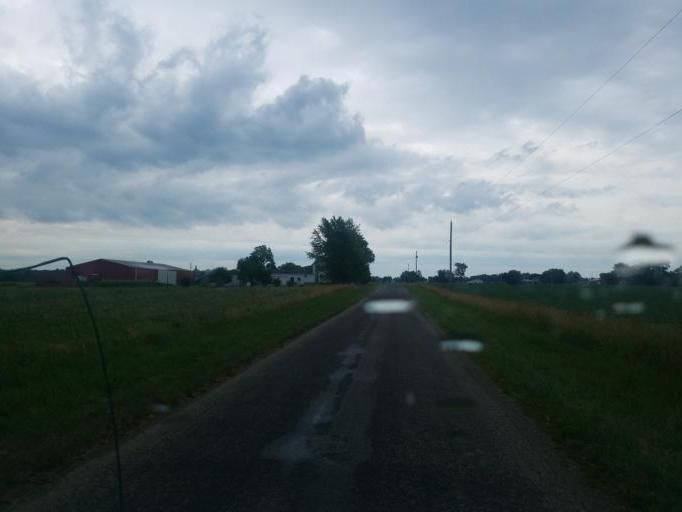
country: US
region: Ohio
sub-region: Defiance County
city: Hicksville
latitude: 41.3681
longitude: -84.7922
